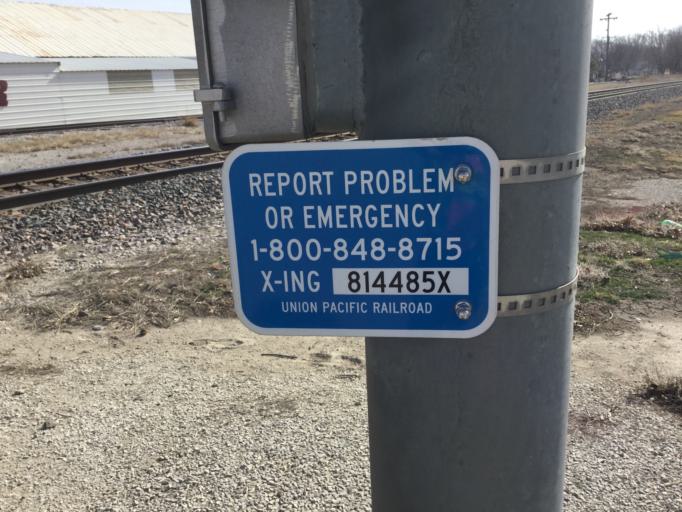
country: US
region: Kansas
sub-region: Nemaha County
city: Seneca
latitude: 39.8730
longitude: -96.2578
